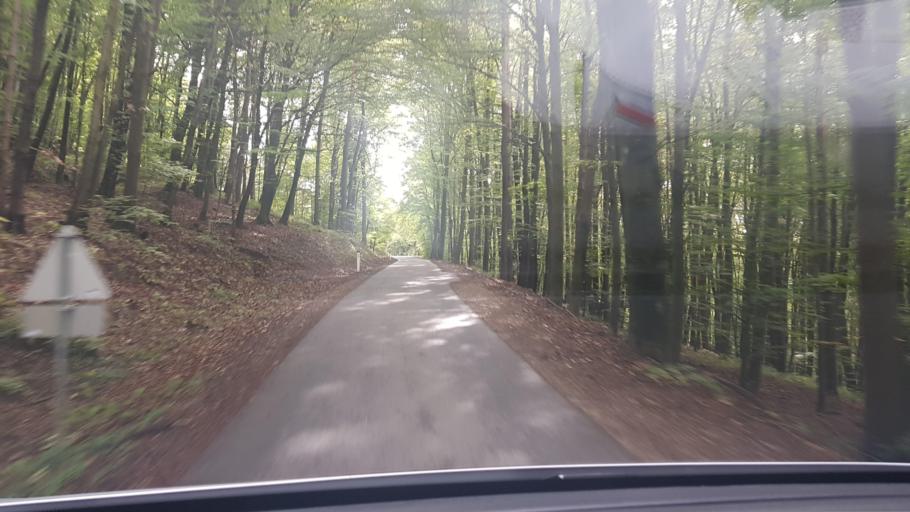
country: AT
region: Styria
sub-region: Politischer Bezirk Leibnitz
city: Sankt Johann im Saggautal
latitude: 46.7171
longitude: 15.4236
